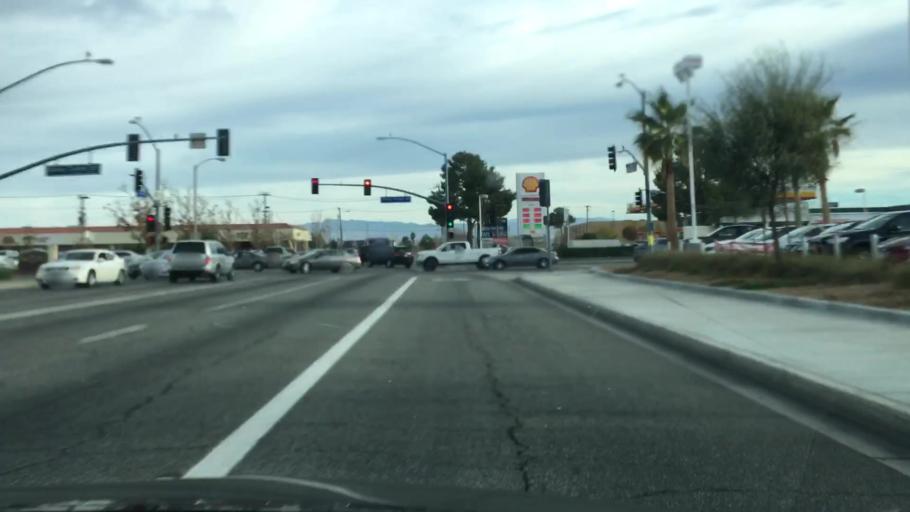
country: US
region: California
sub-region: San Bernardino County
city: Victorville
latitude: 34.5191
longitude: -117.3164
